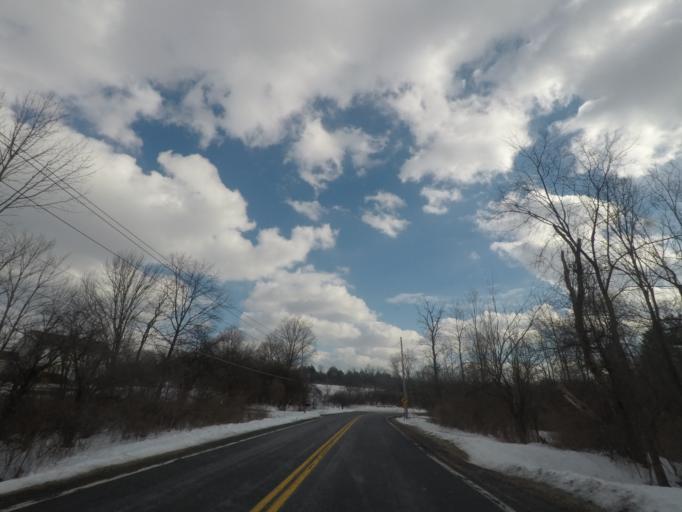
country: US
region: New York
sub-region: Schenectady County
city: Niskayuna
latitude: 42.8202
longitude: -73.8518
